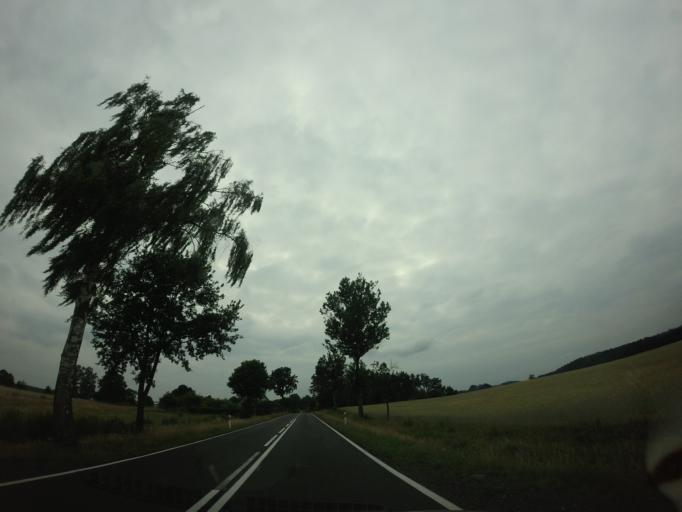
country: PL
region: West Pomeranian Voivodeship
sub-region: Powiat szczecinecki
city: Lubowo
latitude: 53.5901
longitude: 16.3627
